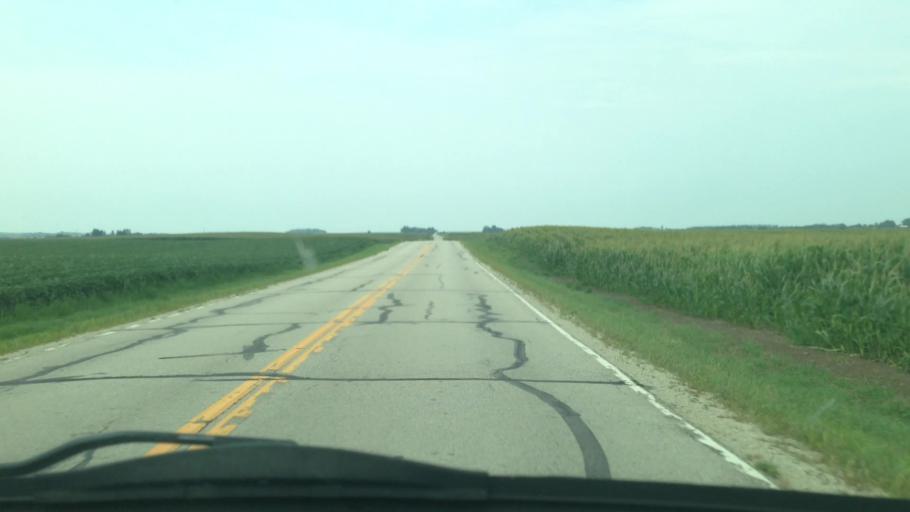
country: US
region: Minnesota
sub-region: Fillmore County
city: Preston
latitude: 43.7836
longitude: -91.9498
